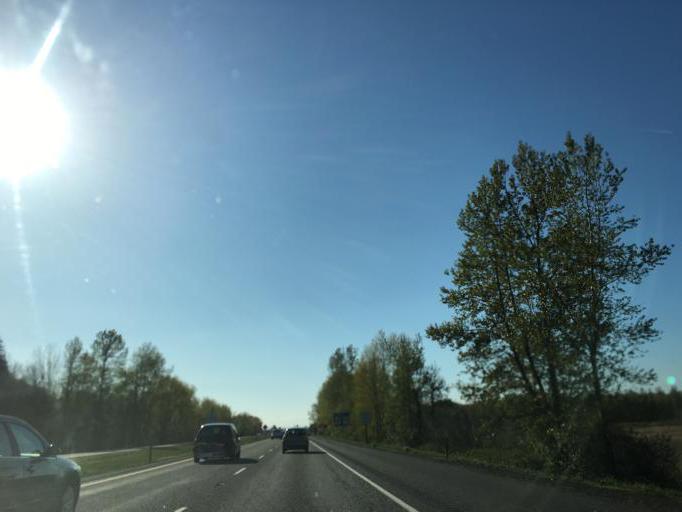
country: US
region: Oregon
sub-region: Multnomah County
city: Troutdale
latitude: 45.5436
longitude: -122.3669
